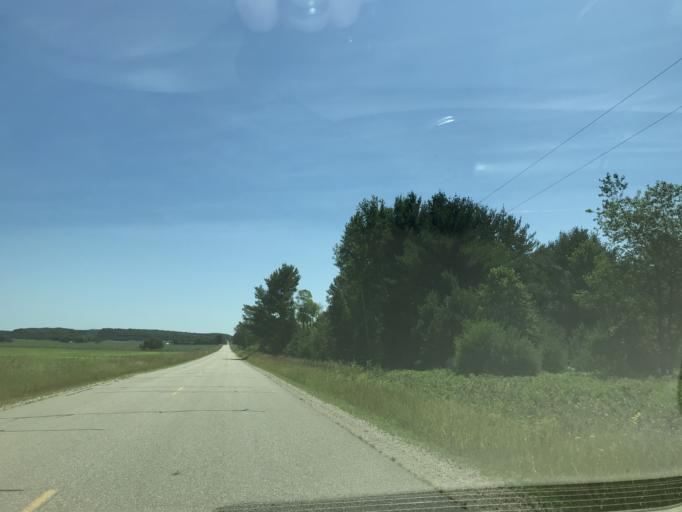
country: US
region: Michigan
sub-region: Missaukee County
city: Lake City
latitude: 44.2795
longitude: -85.0729
